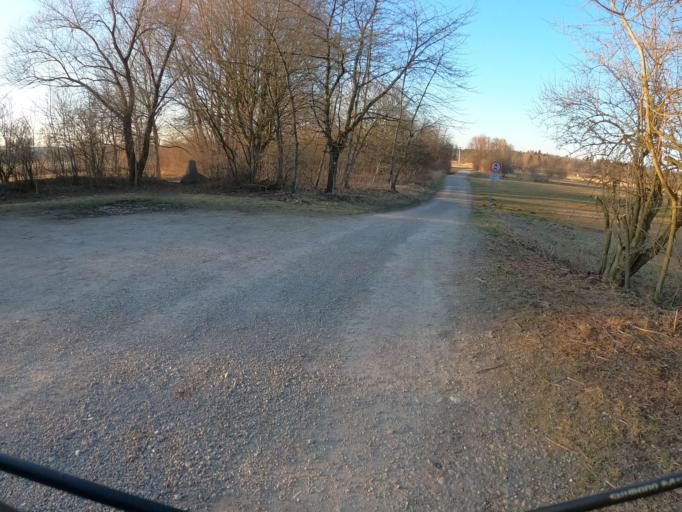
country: DE
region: Bavaria
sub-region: Swabia
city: Nersingen
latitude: 48.4305
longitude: 10.1409
